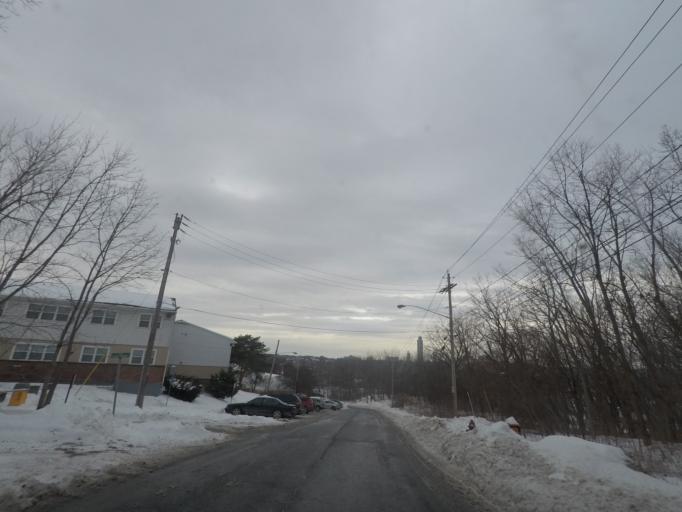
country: US
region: New York
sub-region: Rensselaer County
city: Rensselaer
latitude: 42.6331
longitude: -73.7395
